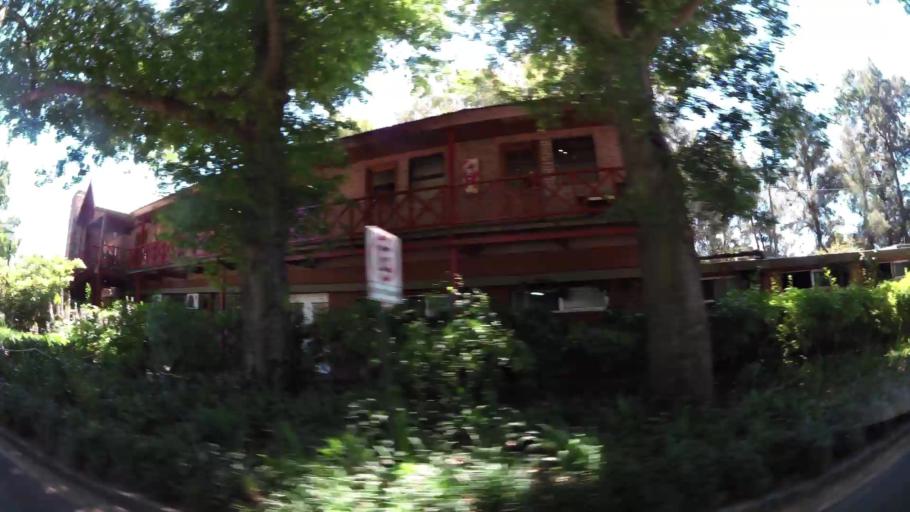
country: AR
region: Buenos Aires
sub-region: Partido de San Isidro
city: San Isidro
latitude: -34.4540
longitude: -58.5102
